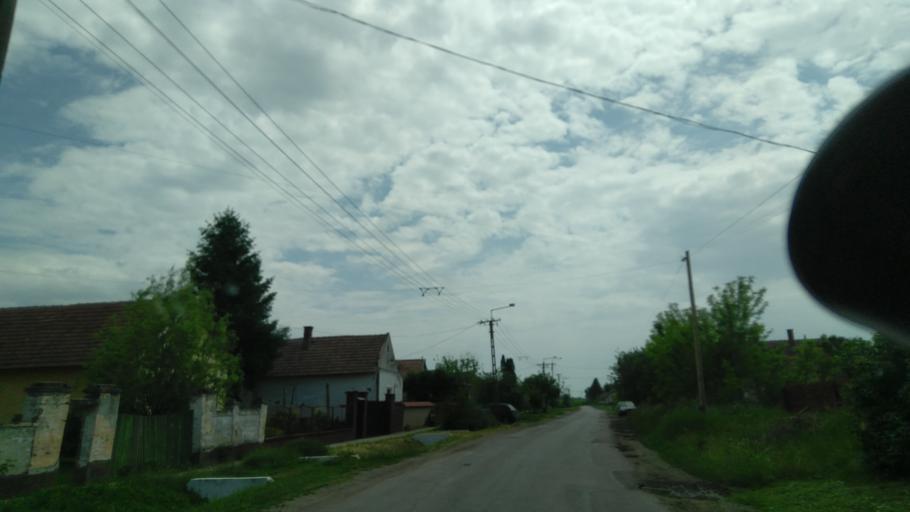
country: HU
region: Hajdu-Bihar
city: Komadi
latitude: 47.0172
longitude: 21.5994
